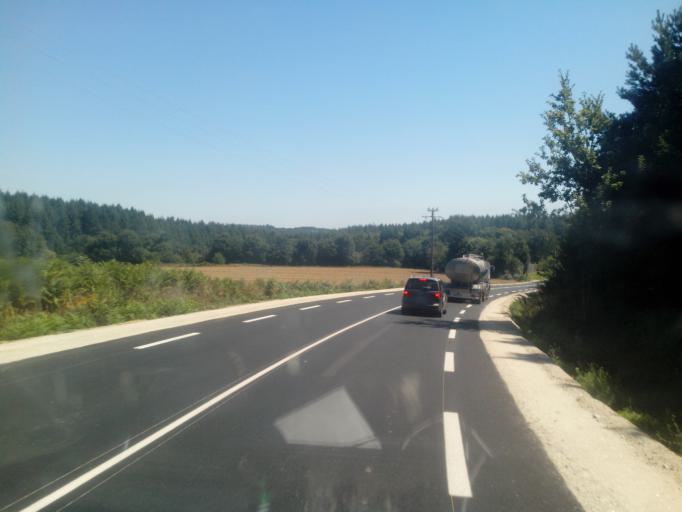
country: FR
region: Brittany
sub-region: Departement du Morbihan
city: Guillac
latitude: 47.8724
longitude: -2.4682
